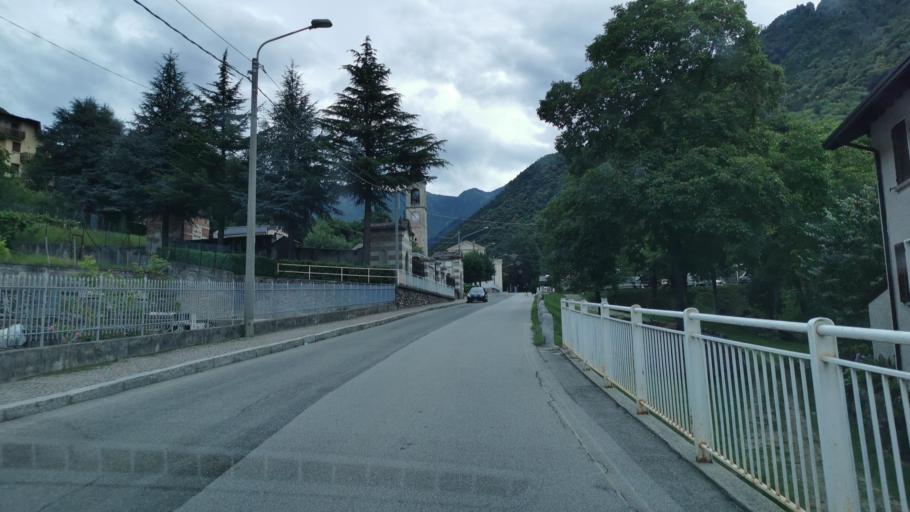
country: IT
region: Lombardy
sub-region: Provincia di Lecco
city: Casargo
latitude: 46.0379
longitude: 9.3864
